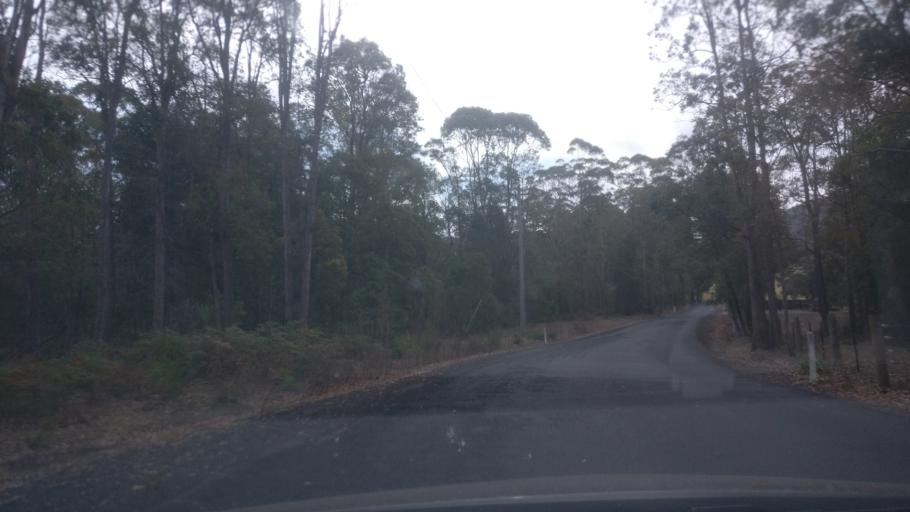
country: AU
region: New South Wales
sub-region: Shoalhaven Shire
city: Kangaroo Valley
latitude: -34.7223
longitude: 150.4744
